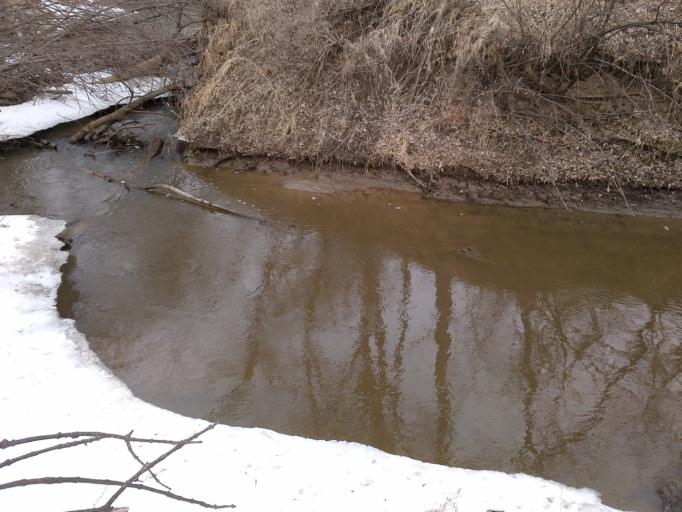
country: US
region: Minnesota
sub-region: Wabasha County
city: Lake City
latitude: 44.4517
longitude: -92.2954
